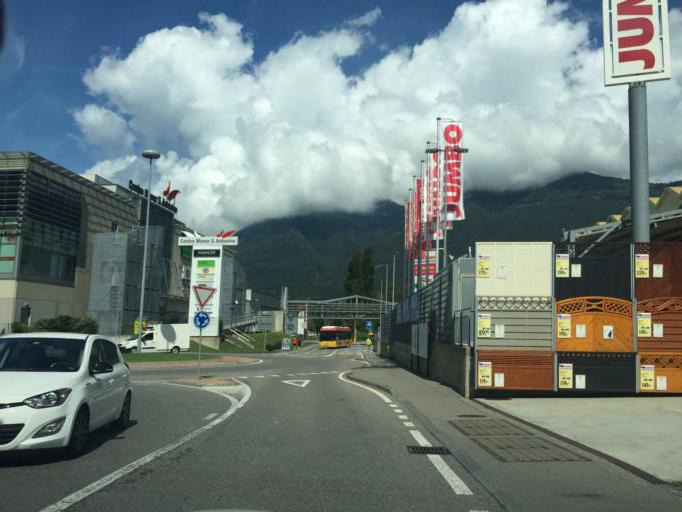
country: CH
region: Ticino
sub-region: Bellinzona District
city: Cadenazzo
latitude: 46.1557
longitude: 8.9678
